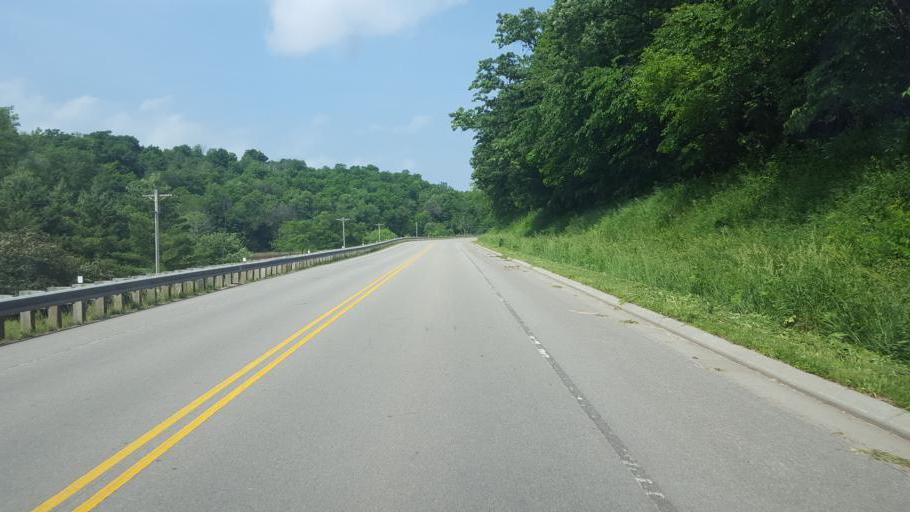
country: US
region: Wisconsin
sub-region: Monroe County
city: Cashton
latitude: 43.7288
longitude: -90.7268
